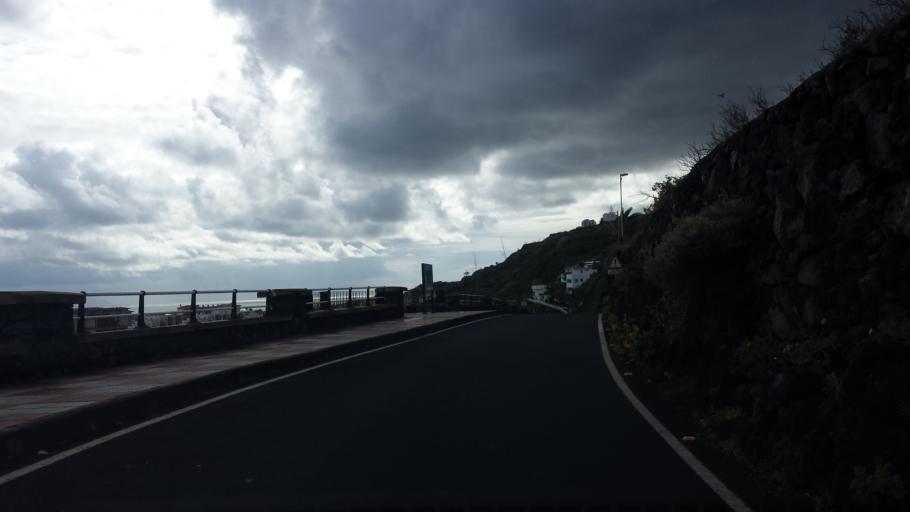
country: ES
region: Canary Islands
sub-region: Provincia de Santa Cruz de Tenerife
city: Brena Alta
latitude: 28.6553
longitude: -17.7627
